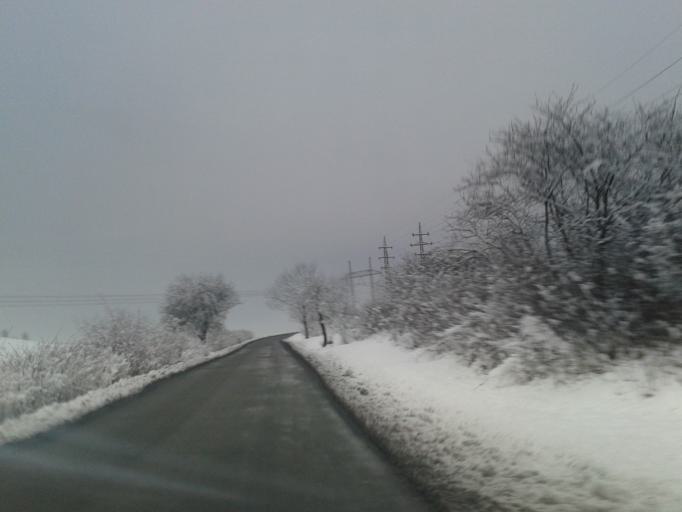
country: CZ
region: Central Bohemia
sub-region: Okres Beroun
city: Beroun
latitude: 49.9250
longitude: 14.0918
